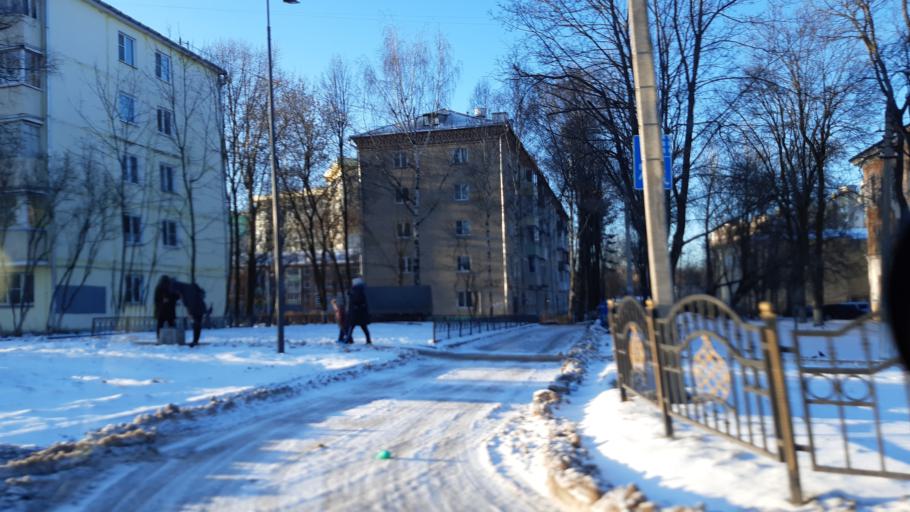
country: RU
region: Moskovskaya
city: Sergiyev Posad
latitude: 56.3240
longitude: 38.1463
